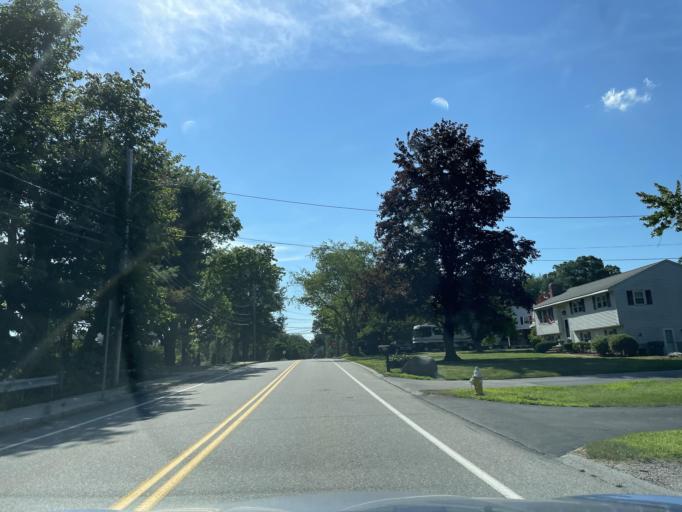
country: US
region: Massachusetts
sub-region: Worcester County
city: Northbridge
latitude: 42.1546
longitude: -71.6783
